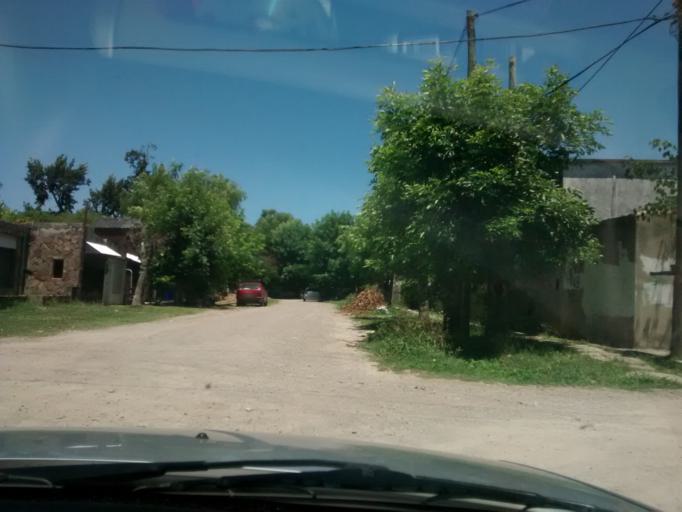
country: AR
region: Buenos Aires
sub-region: Partido de Berisso
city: Berisso
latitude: -34.8805
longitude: -57.8489
